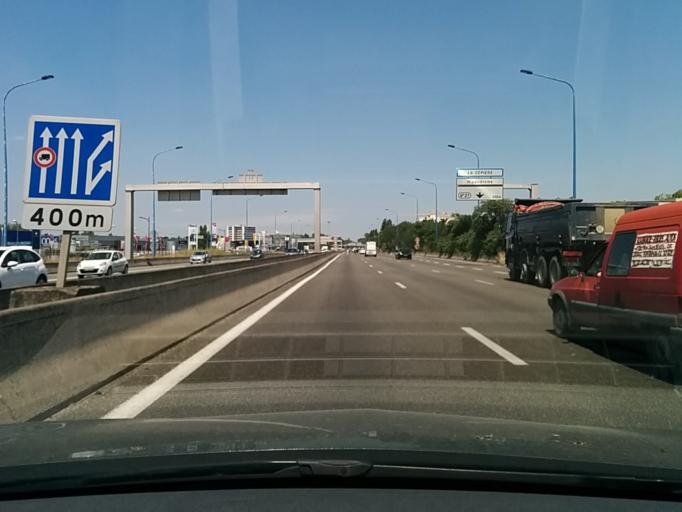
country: FR
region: Midi-Pyrenees
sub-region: Departement de la Haute-Garonne
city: Toulouse
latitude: 43.5793
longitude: 1.4063
